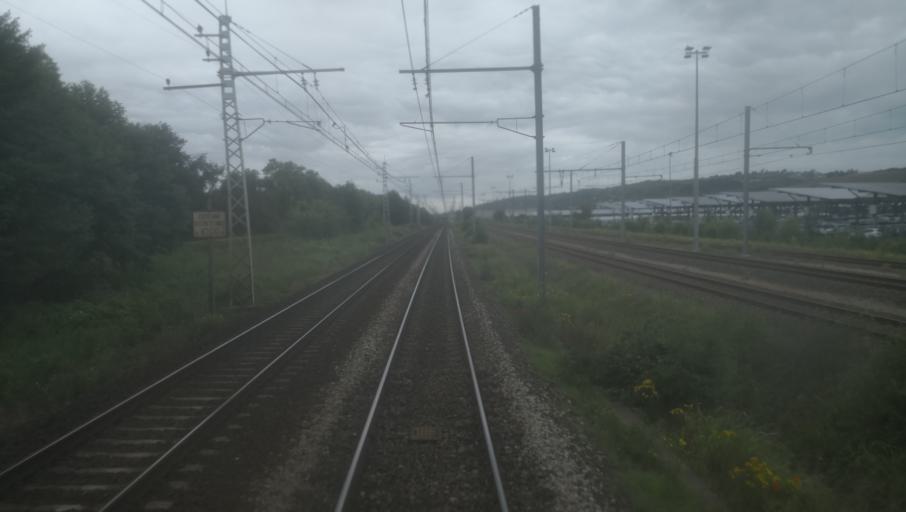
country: FR
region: Midi-Pyrenees
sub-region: Departement de la Haute-Garonne
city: Castelnau-d'Estretefonds
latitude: 43.7779
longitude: 1.3489
